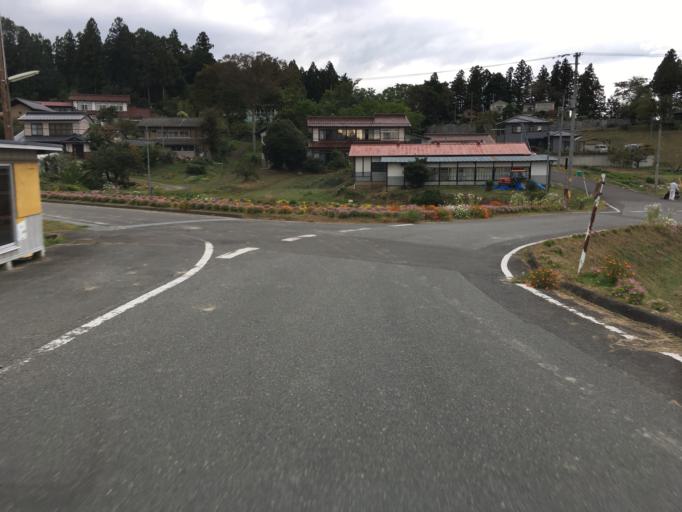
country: JP
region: Fukushima
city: Fukushima-shi
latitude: 37.6622
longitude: 140.5211
